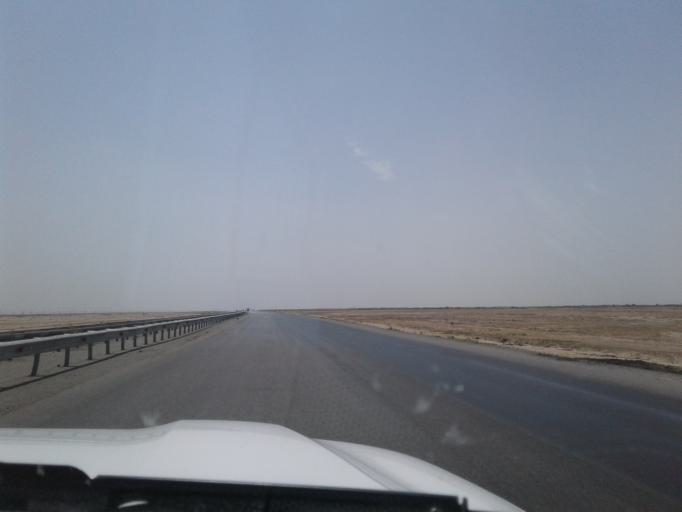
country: TM
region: Ahal
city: Tejen
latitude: 37.3469
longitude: 60.4041
